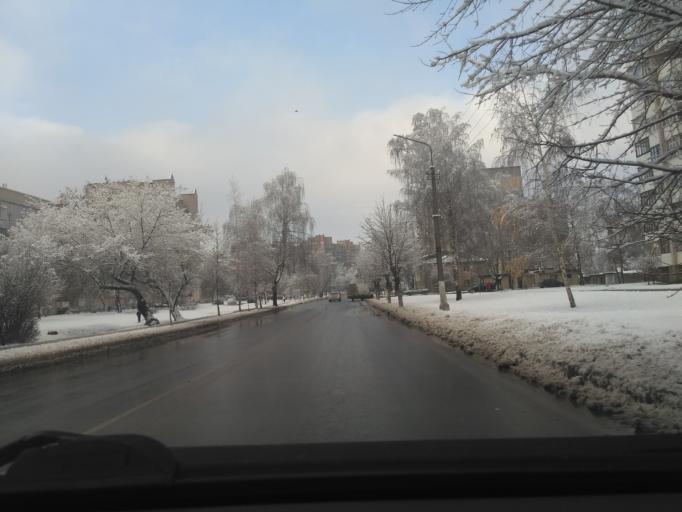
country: BY
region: Minsk
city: Horad Barysaw
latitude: 54.2183
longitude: 28.4969
